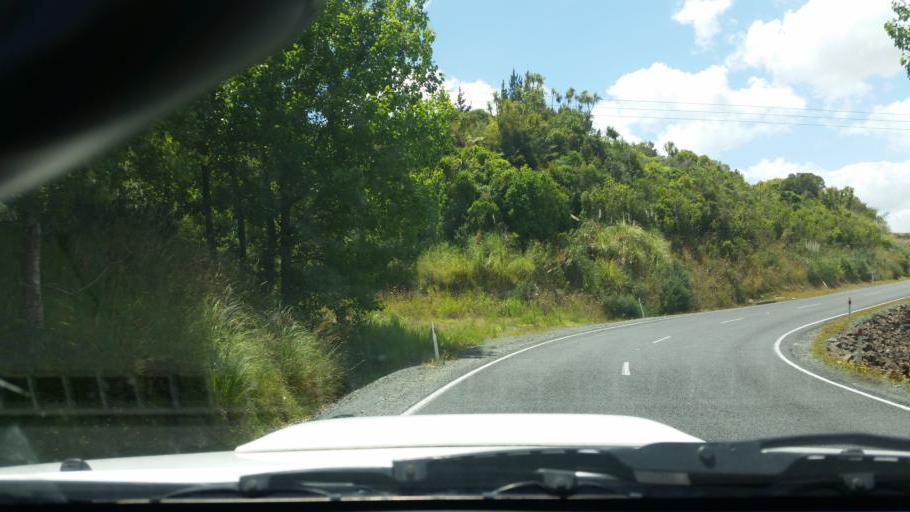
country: NZ
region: Northland
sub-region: Whangarei
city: Ruakaka
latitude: -36.0826
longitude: 174.2391
